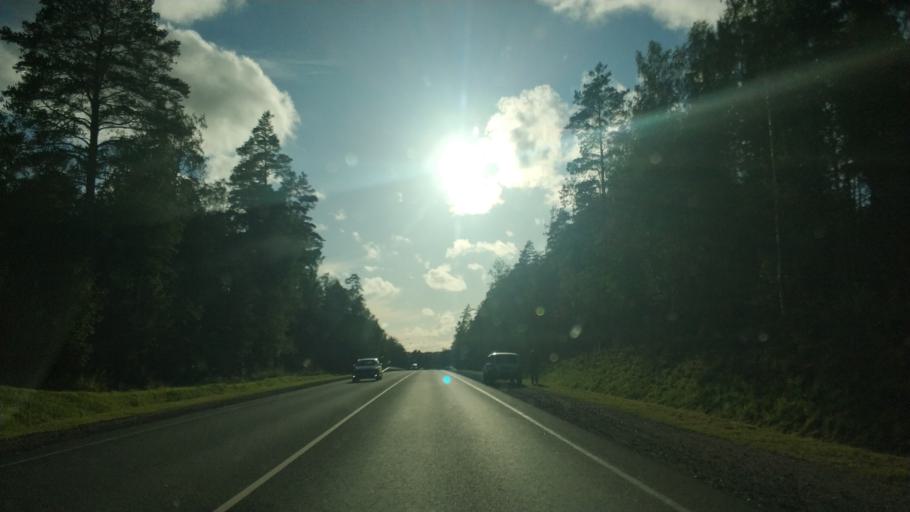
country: RU
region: Leningrad
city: Sapernoye
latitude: 60.7158
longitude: 30.0046
